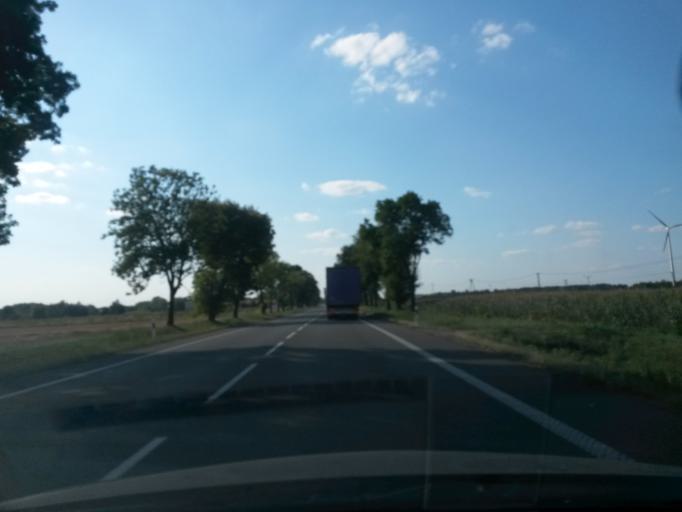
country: PL
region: Masovian Voivodeship
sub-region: Powiat sierpecki
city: Sierpc
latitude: 52.8398
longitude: 19.7299
